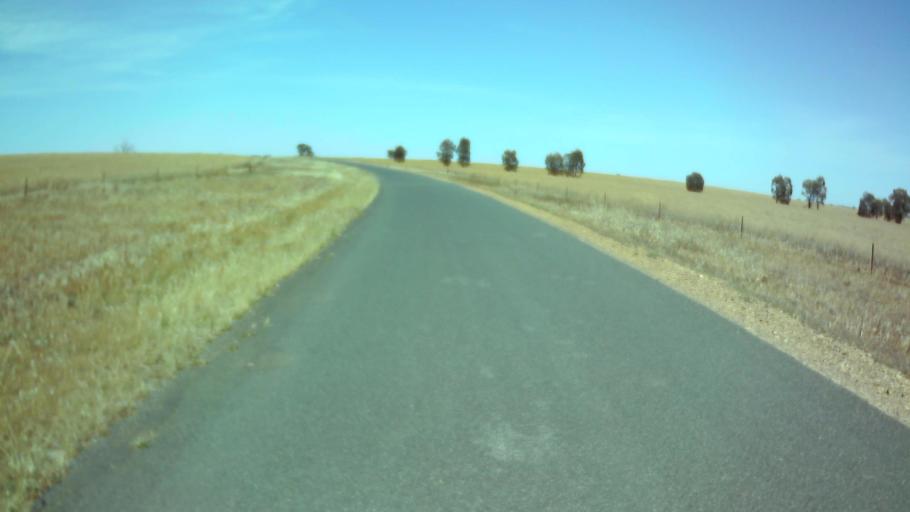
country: AU
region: New South Wales
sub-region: Weddin
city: Grenfell
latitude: -33.8555
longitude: 147.9330
